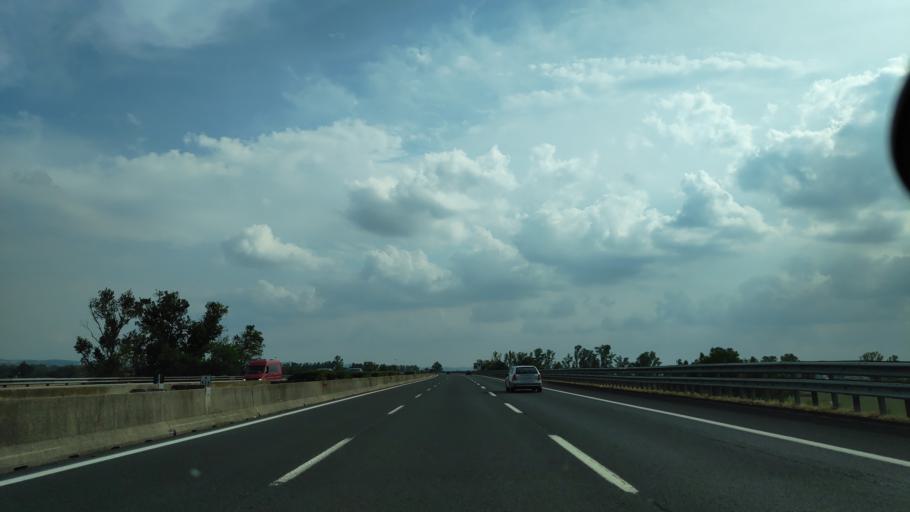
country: IT
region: Latium
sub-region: Citta metropolitana di Roma Capitale
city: Bivio di Capanelle
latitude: 42.1363
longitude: 12.6189
